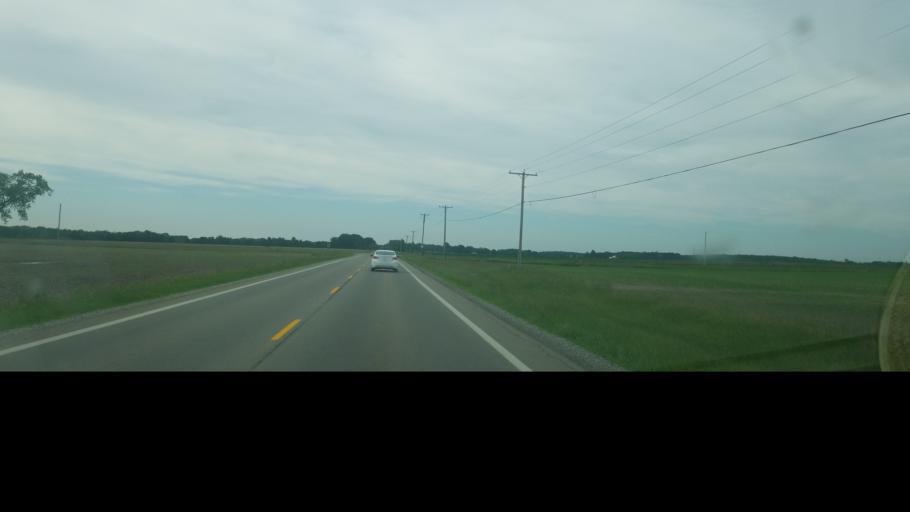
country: US
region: Ohio
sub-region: Delaware County
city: Ashley
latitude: 40.4370
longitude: -82.9523
